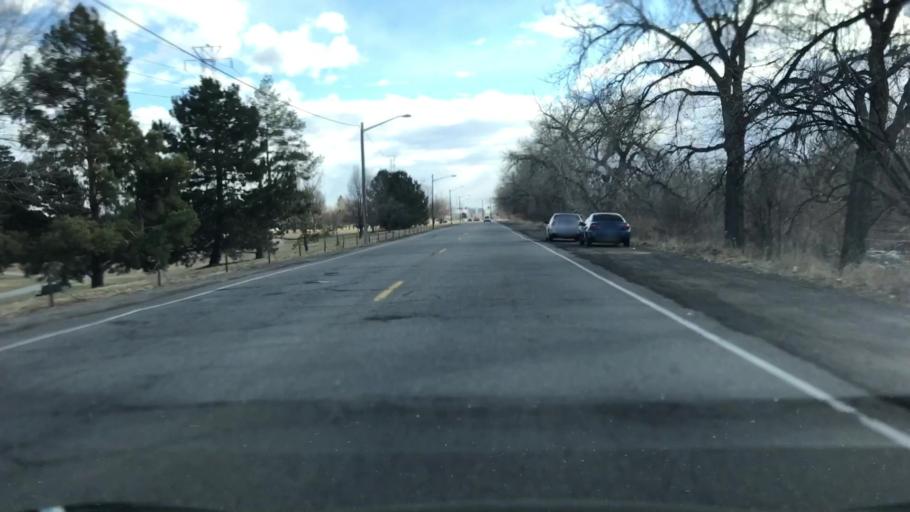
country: US
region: Colorado
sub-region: Arapahoe County
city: Glendale
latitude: 39.6936
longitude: -104.9168
